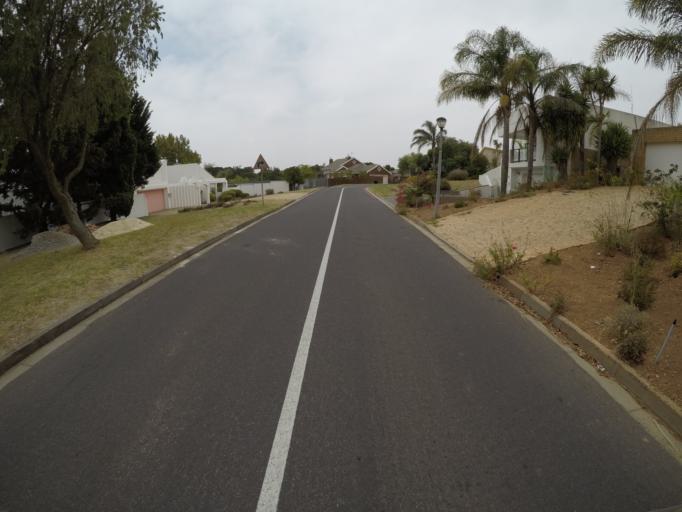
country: ZA
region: Western Cape
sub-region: City of Cape Town
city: Kraaifontein
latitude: -33.8686
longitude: 18.6442
